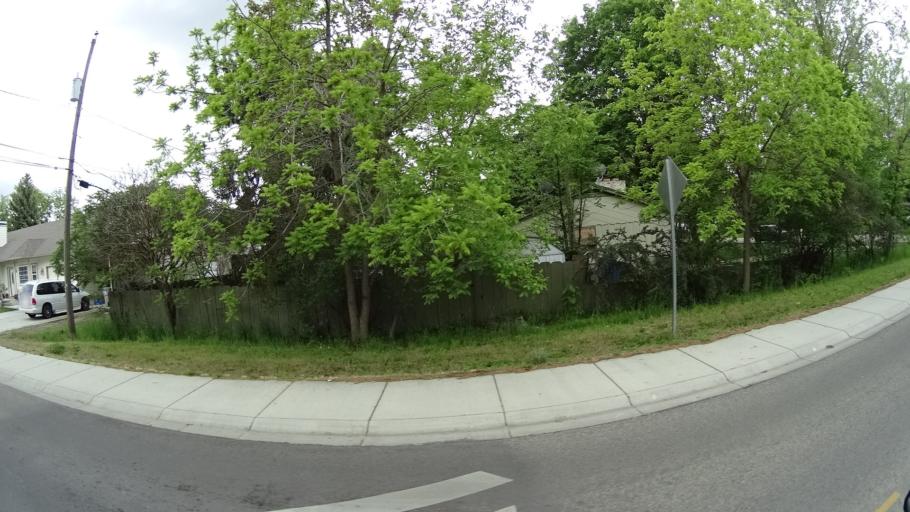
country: US
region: Idaho
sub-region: Ada County
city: Garden City
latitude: 43.6555
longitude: -116.2444
